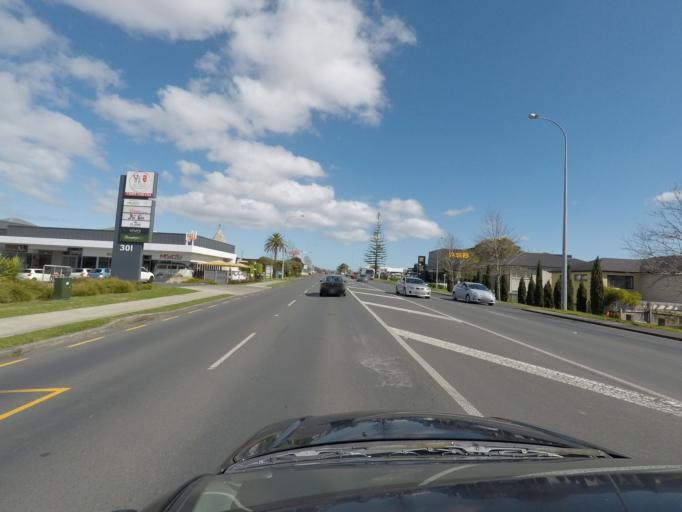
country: NZ
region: Auckland
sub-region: Auckland
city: Rosebank
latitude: -36.8531
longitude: 174.6301
